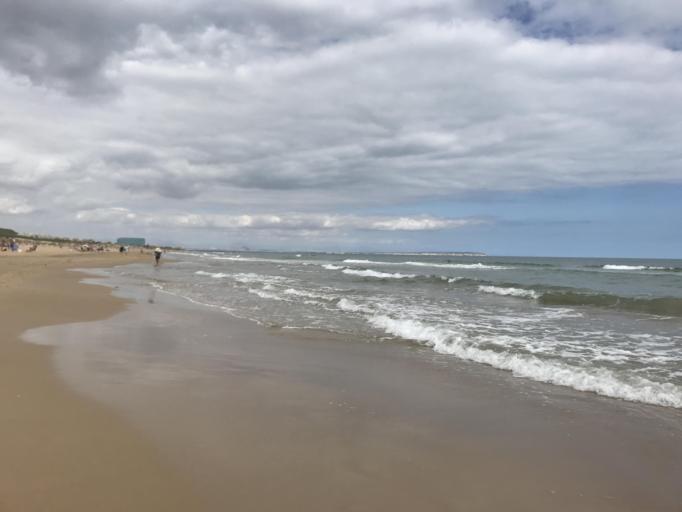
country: ES
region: Valencia
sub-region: Provincia de Alicante
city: Guardamar del Segura
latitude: 38.0456
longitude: -0.6513
